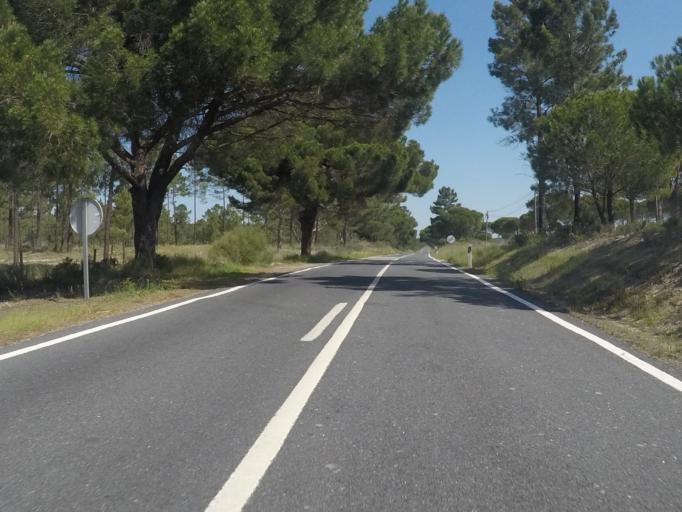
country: PT
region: Setubal
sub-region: Grandola
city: Grandola
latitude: 38.2849
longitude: -8.7262
